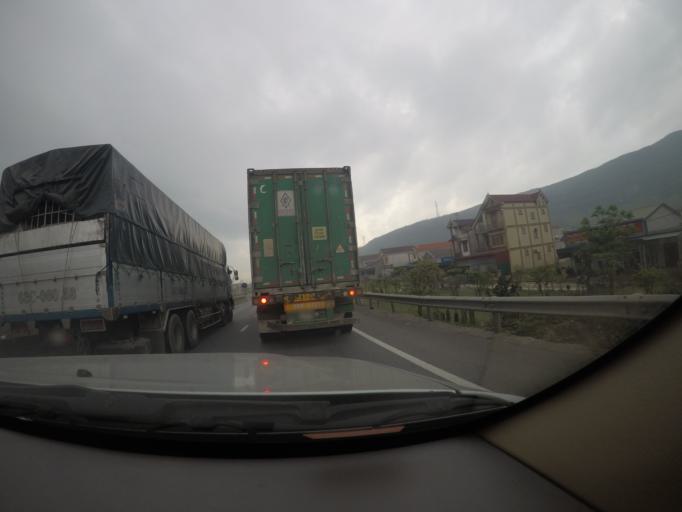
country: VN
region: Ha Tinh
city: Ky Anh
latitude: 17.9936
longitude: 106.4684
